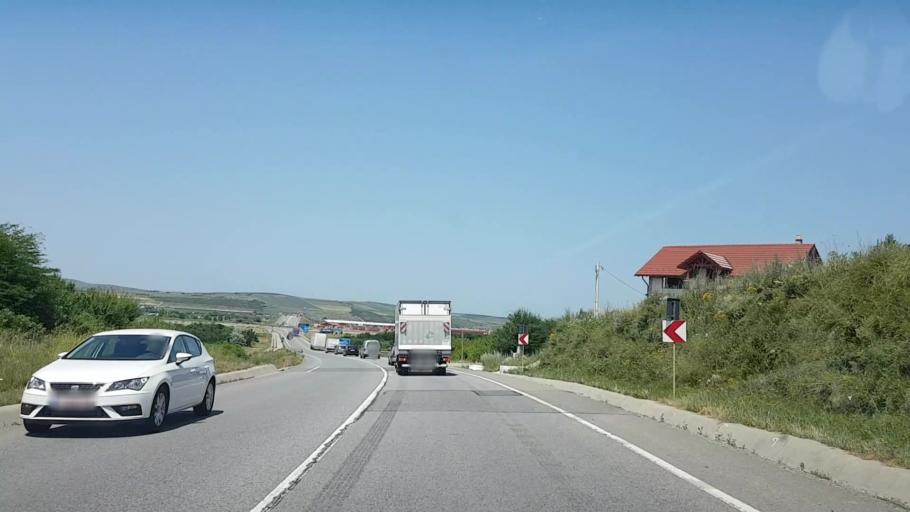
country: RO
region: Cluj
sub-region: Comuna Apahida
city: Dezmir
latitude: 46.7729
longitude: 23.7015
